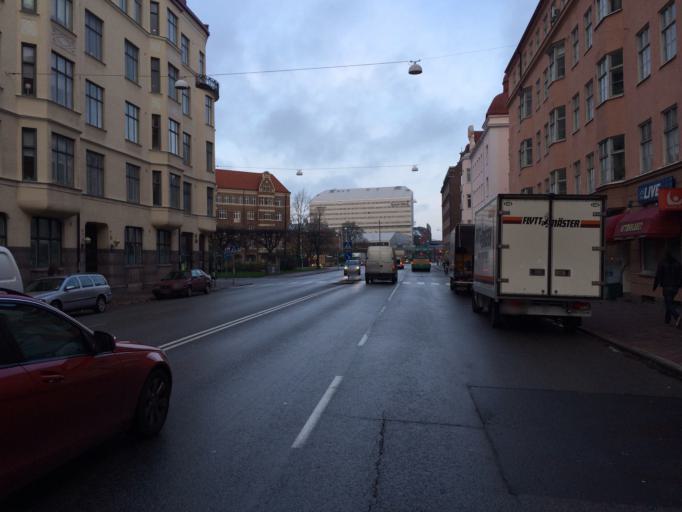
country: SE
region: Skane
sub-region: Malmo
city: Malmoe
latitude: 55.5974
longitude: 13.0111
